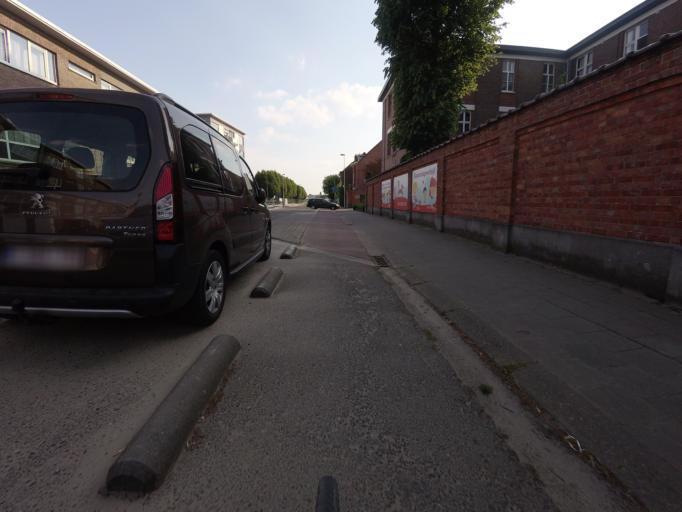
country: BE
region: Flanders
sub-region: Provincie Antwerpen
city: Mortsel
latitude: 51.1955
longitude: 4.4519
